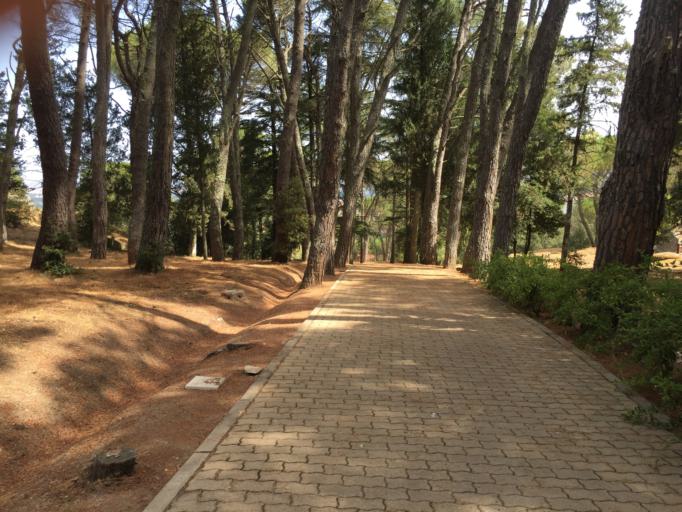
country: IT
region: Sardinia
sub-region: Provincia di Olbia-Tempio
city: Tempio Pausania
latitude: 40.8978
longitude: 9.0972
